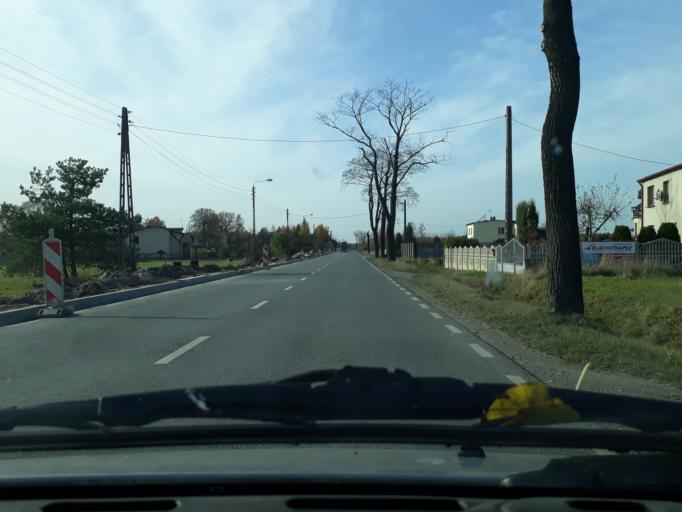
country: PL
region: Silesian Voivodeship
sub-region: Powiat lubliniecki
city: Psary
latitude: 50.5769
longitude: 18.9972
